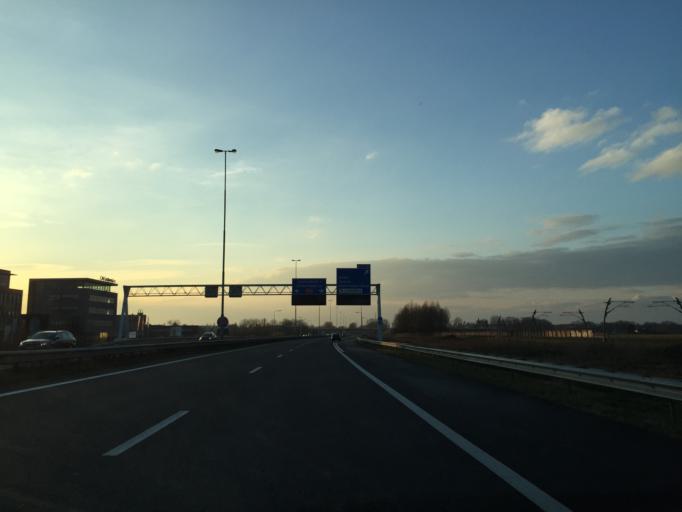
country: NL
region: North Brabant
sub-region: Gemeente Woudrichem
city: Woudrichem
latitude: 51.8422
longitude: 5.0131
